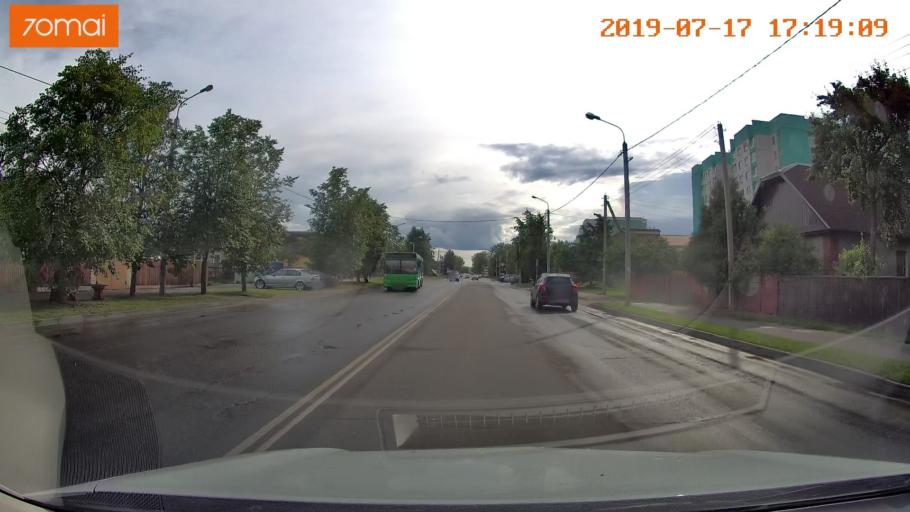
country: BY
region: Mogilev
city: Babruysk
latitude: 53.1582
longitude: 29.1942
